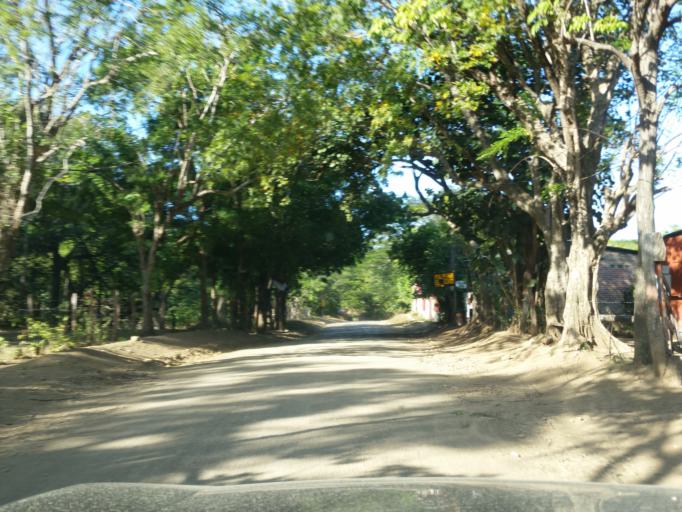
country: NI
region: Rivas
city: San Juan del Sur
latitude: 11.2023
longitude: -85.8042
